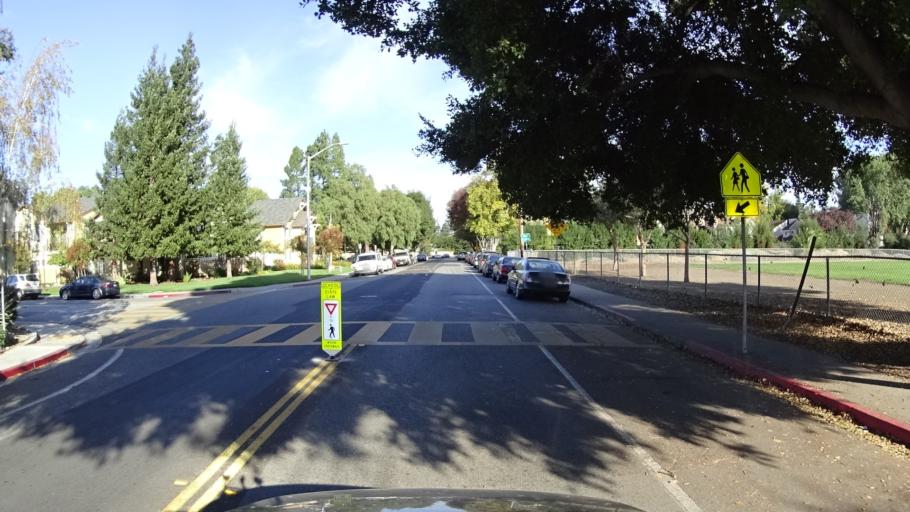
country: US
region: California
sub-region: Santa Clara County
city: Santa Clara
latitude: 37.3679
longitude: -121.9745
